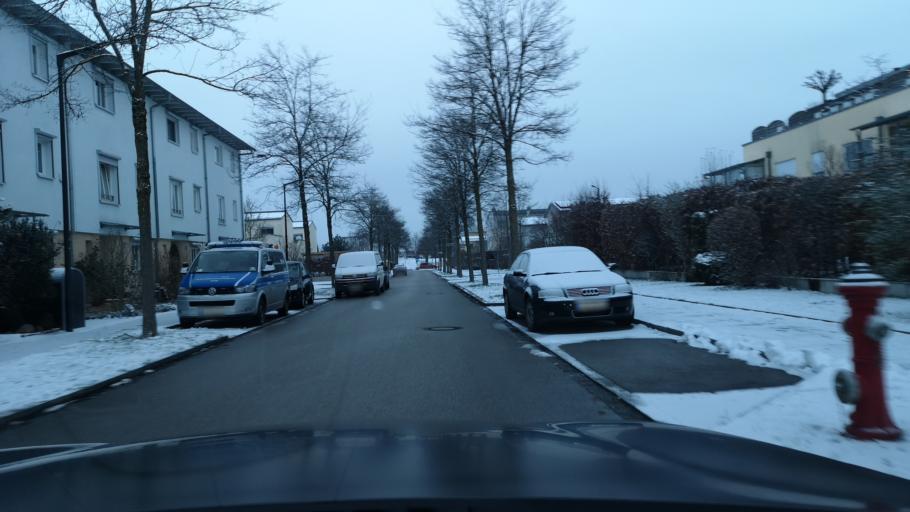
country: DE
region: Bavaria
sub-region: Upper Bavaria
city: Poing
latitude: 48.1741
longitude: 11.7984
